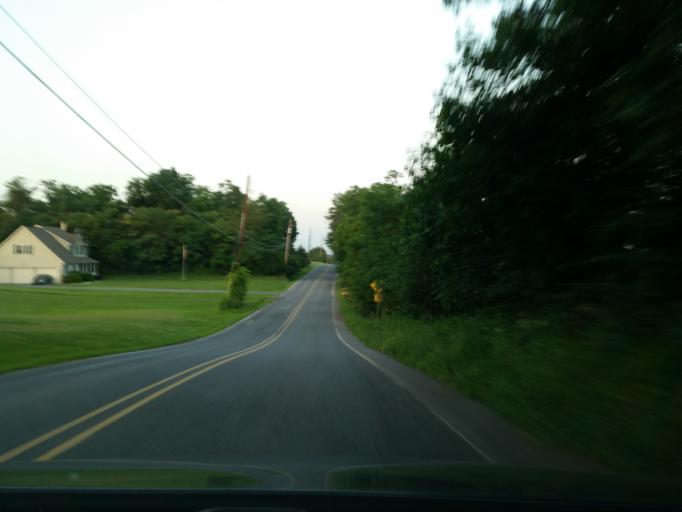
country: US
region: Pennsylvania
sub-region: Lebanon County
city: Jonestown
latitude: 40.4186
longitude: -76.5169
